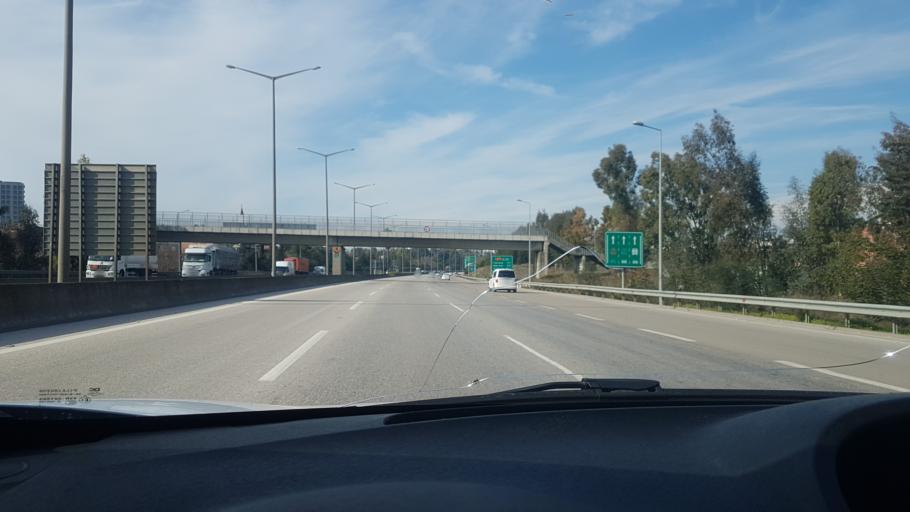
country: TR
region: Adana
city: Adana
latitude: 37.0233
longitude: 35.3382
